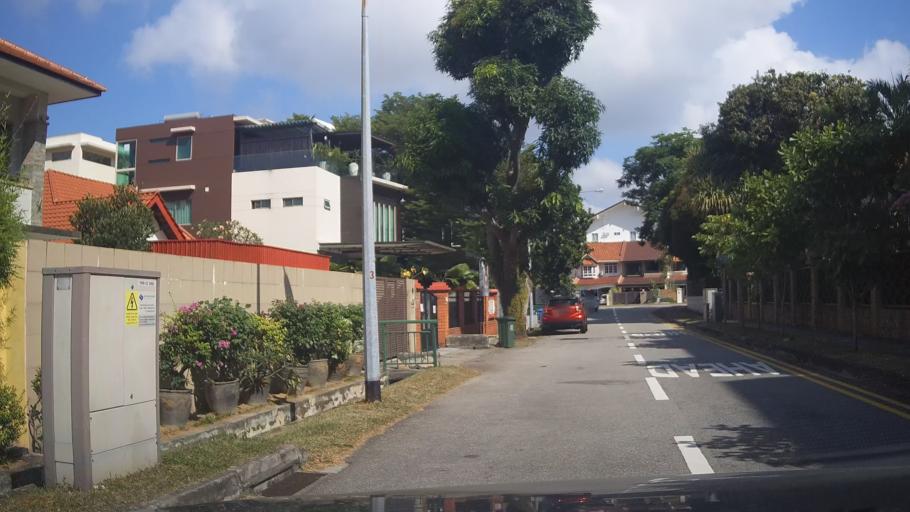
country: SG
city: Singapore
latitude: 1.3135
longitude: 103.9356
